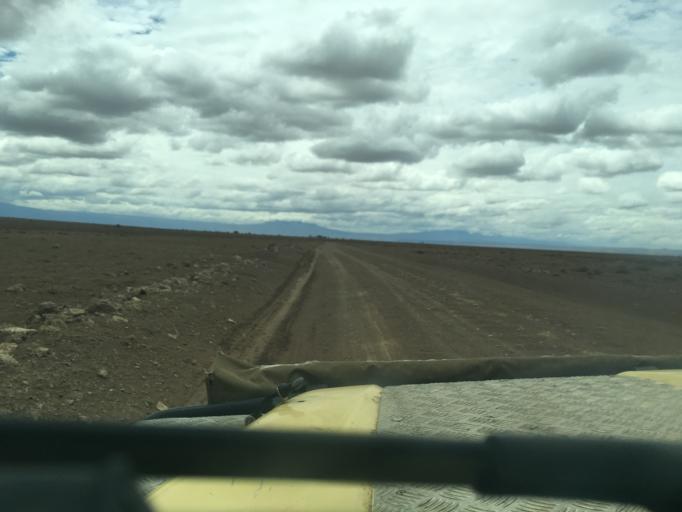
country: TZ
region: Arusha
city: Mto wa Mbu
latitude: -2.9074
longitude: 36.0612
